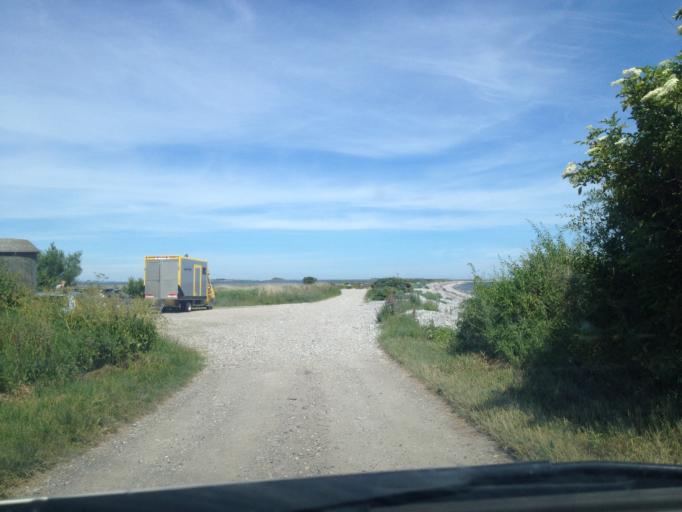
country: DK
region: Central Jutland
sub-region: Samso Kommune
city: Tranebjerg
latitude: 55.8817
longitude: 10.6775
